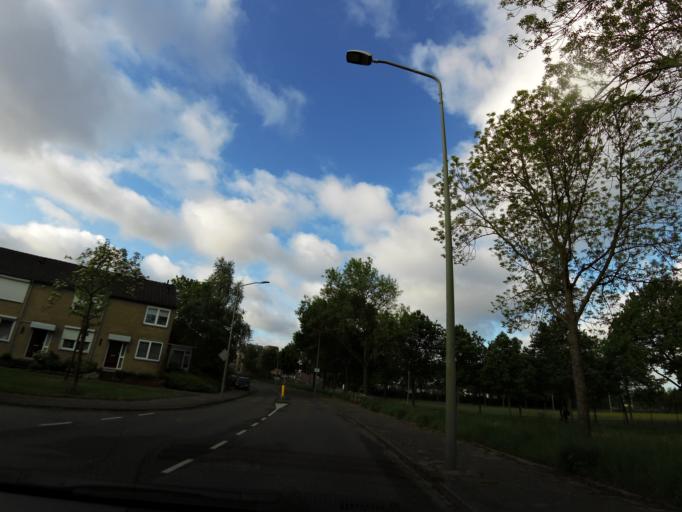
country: NL
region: Limburg
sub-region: Gemeente Brunssum
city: Brunssum
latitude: 50.9249
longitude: 5.9625
